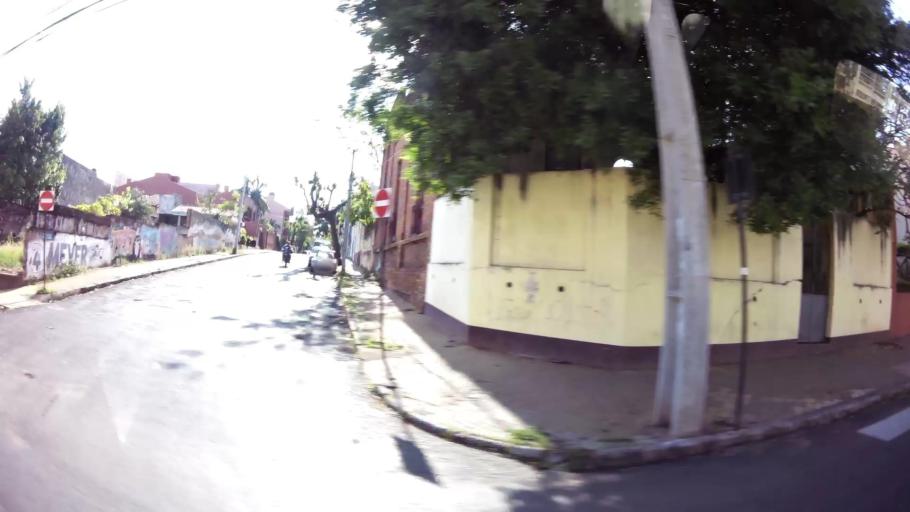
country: PY
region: Asuncion
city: Asuncion
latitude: -25.2826
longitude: -57.6161
